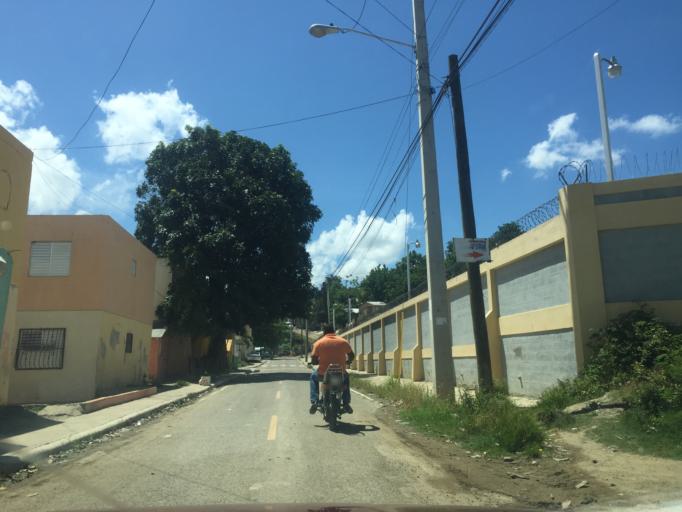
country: DO
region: Santiago
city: Santiago de los Caballeros
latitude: 19.4413
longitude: -70.7438
